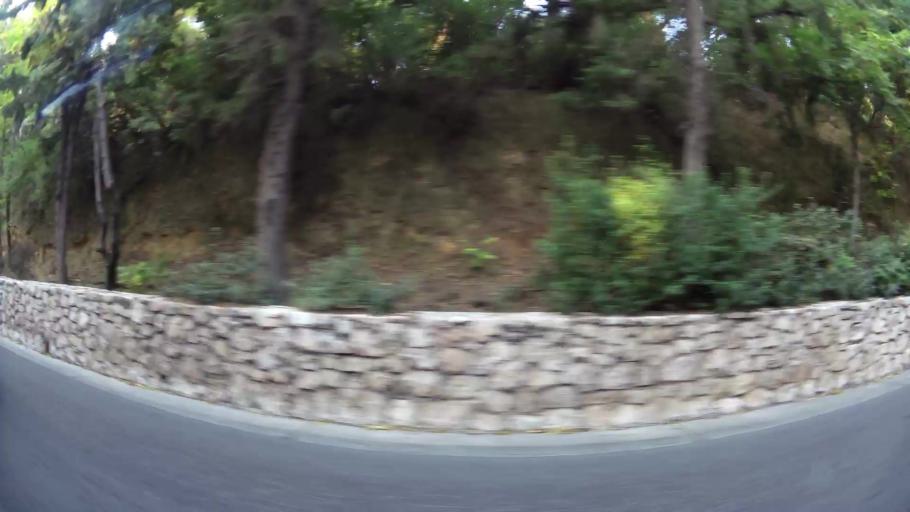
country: GR
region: Attica
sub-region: Nomarchia Athinas
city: Vyronas
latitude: 37.9829
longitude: 23.7513
